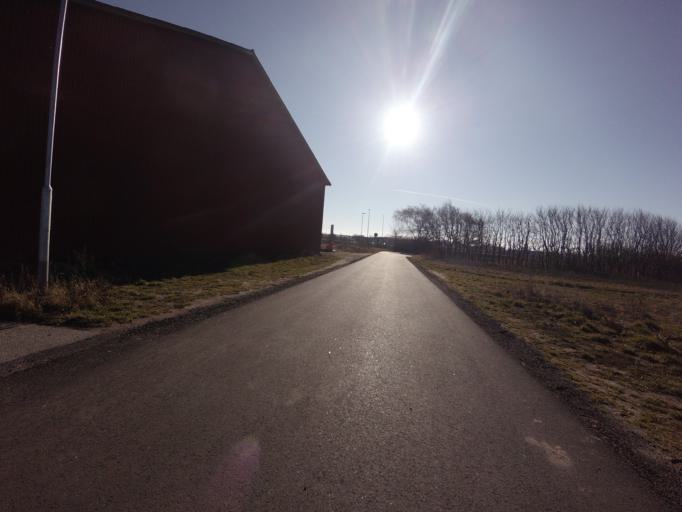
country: SE
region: Skane
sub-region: Vellinge Kommun
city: Hollviken
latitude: 55.4263
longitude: 12.9583
